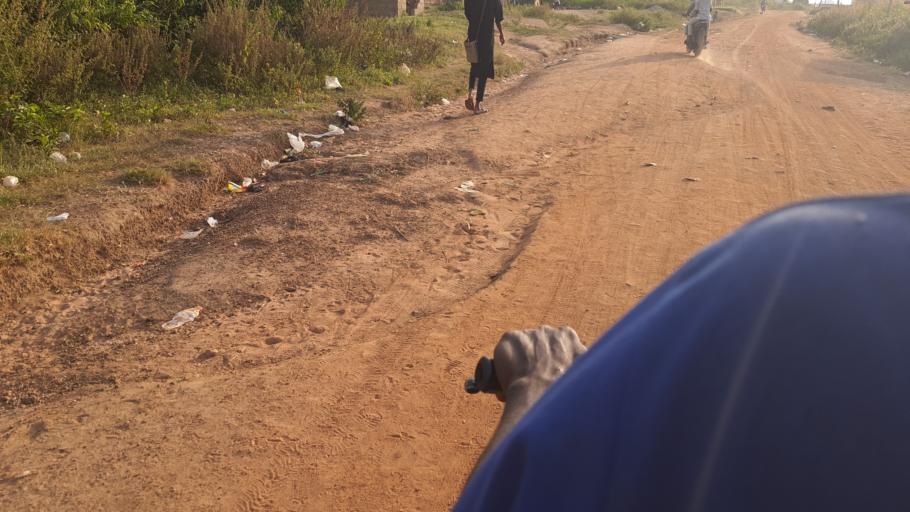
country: NG
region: Osun
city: Iwo
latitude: 7.6201
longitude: 4.1589
